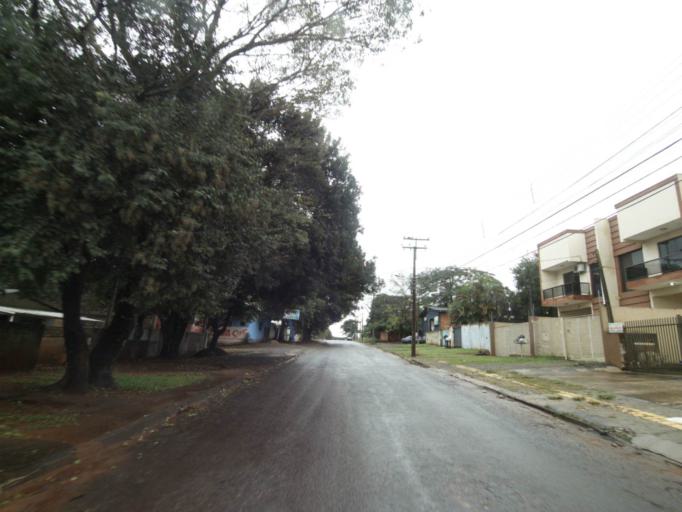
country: PY
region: Alto Parana
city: Ciudad del Este
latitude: -25.5136
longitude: -54.5806
